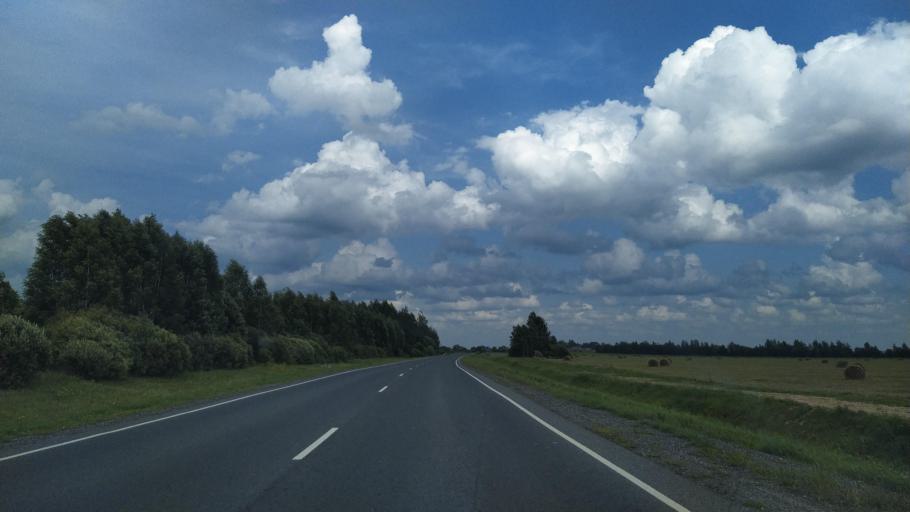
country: RU
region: Novgorod
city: Sol'tsy
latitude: 58.0786
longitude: 30.0760
